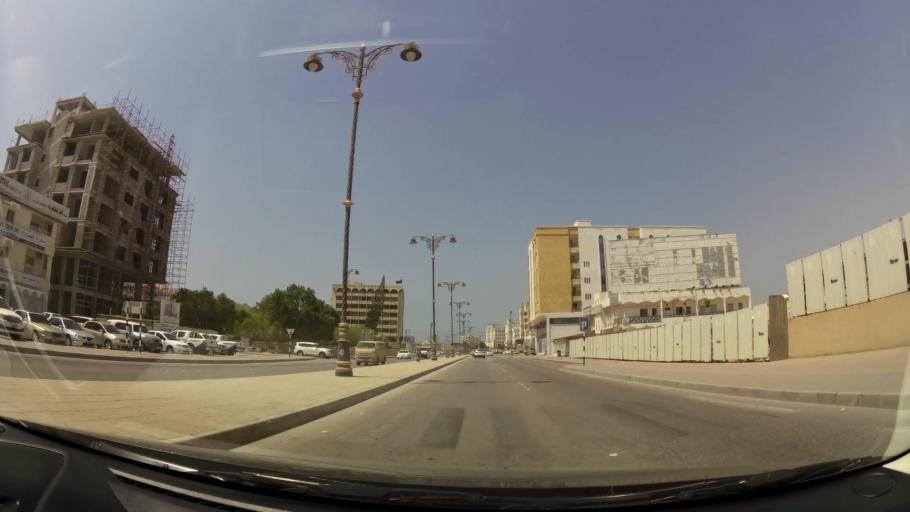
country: OM
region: Zufar
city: Salalah
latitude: 17.0227
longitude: 54.1112
